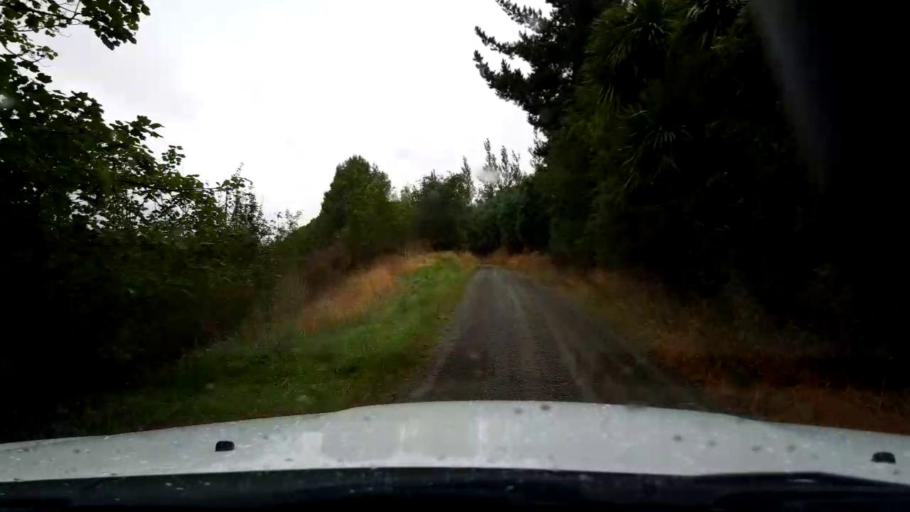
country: NZ
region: Canterbury
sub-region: Timaru District
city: Pleasant Point
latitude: -44.1076
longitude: 171.1347
